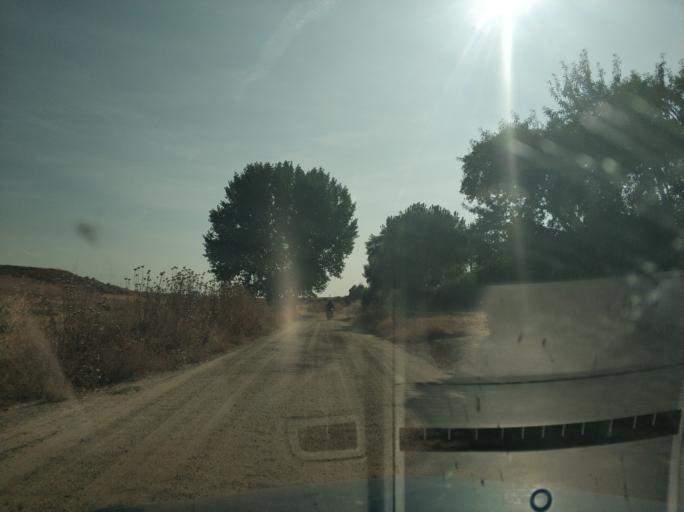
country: ES
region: Castille and Leon
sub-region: Provincia de Salamanca
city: Villamayor
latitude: 41.0112
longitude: -5.6744
